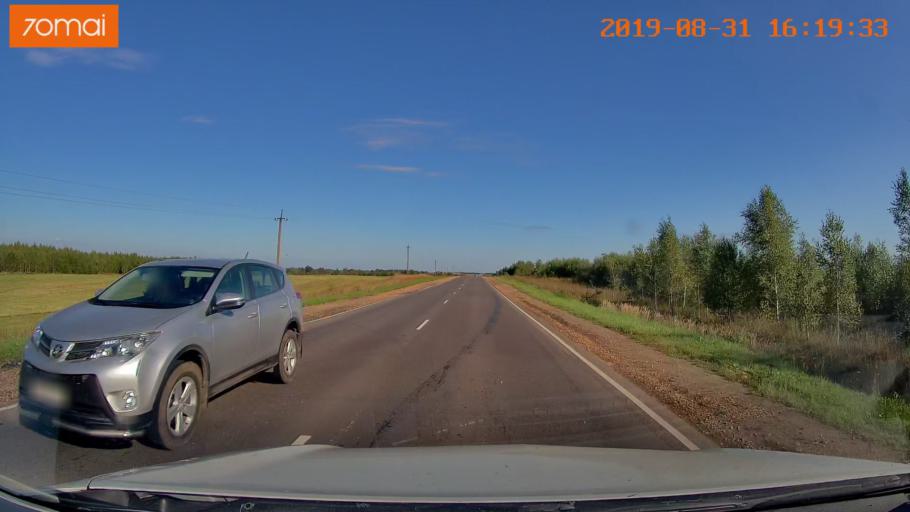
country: RU
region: Kaluga
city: Nikola-Lenivets
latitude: 54.5283
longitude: 35.5816
